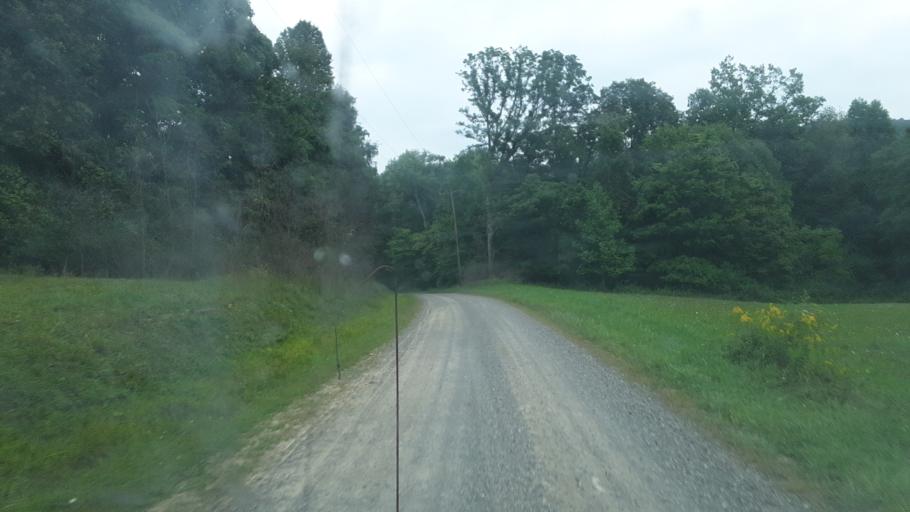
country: US
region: Pennsylvania
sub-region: Jefferson County
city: Punxsutawney
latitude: 40.9536
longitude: -79.1498
